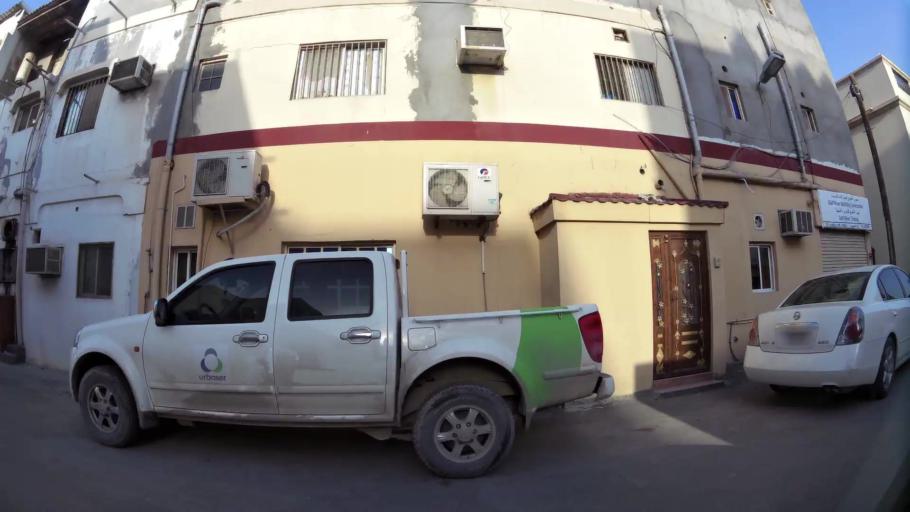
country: BH
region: Northern
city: Madinat `Isa
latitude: 26.1921
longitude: 50.4874
